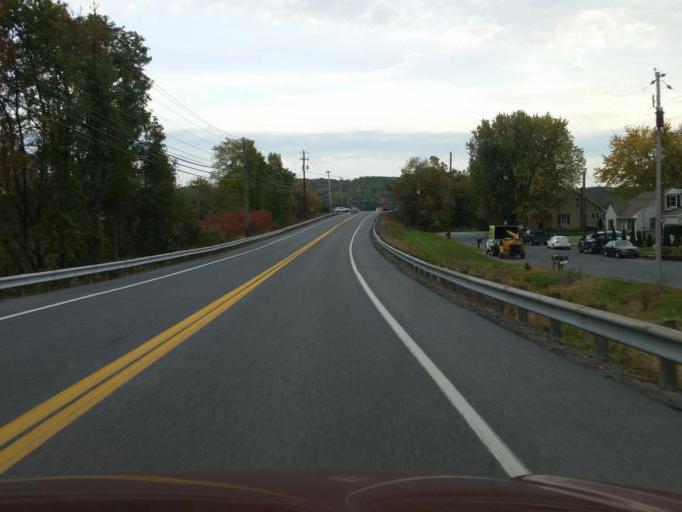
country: US
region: Pennsylvania
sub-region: Dauphin County
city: Hummelstown
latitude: 40.2611
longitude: -76.7012
